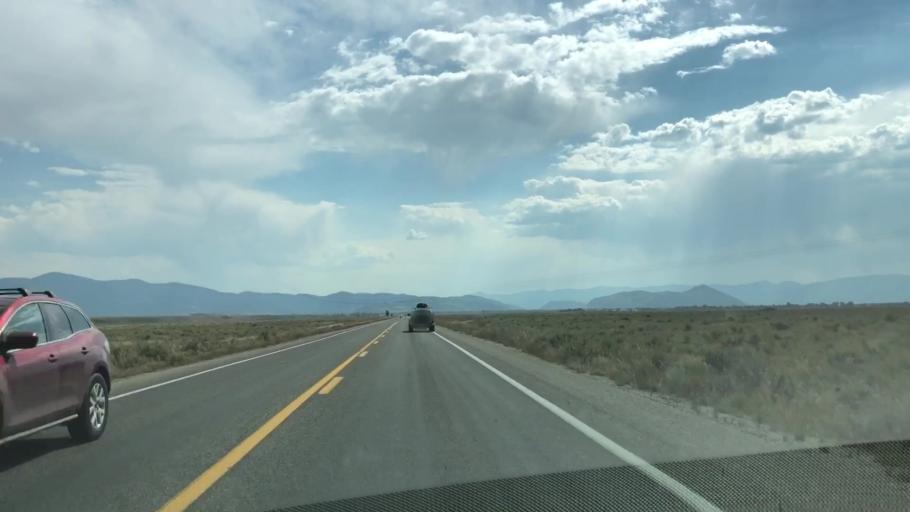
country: US
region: Wyoming
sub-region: Teton County
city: Jackson
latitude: 43.6311
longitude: -110.7181
